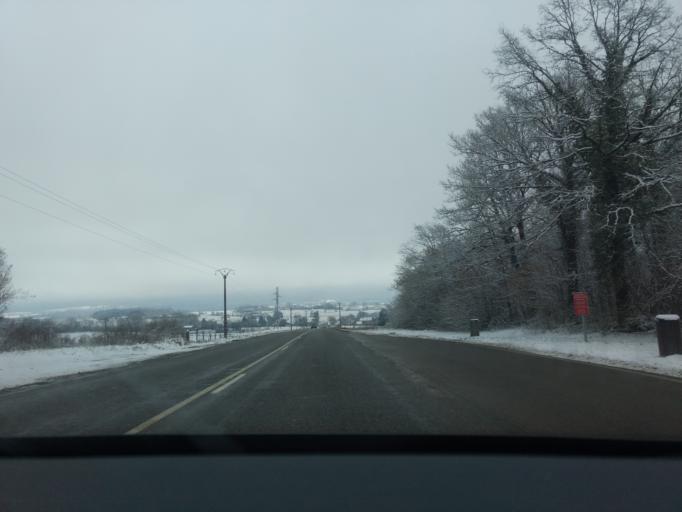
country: FR
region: Franche-Comte
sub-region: Departement du Jura
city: Champagnole
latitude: 46.7804
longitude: 5.8865
